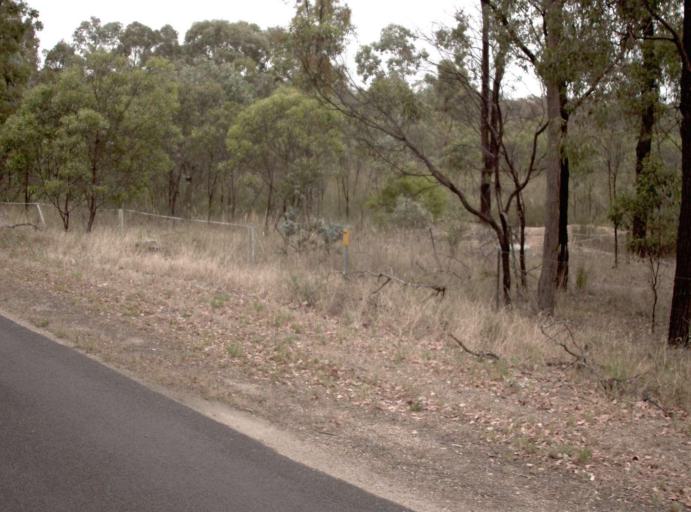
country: AU
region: Victoria
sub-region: Wellington
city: Heyfield
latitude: -37.9619
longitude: 146.7745
